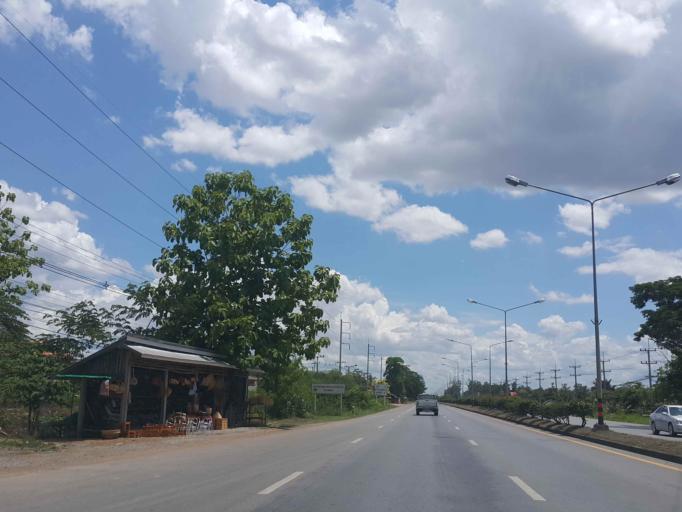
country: TH
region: Phrae
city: Nong Muang Khai
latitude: 18.2488
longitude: 100.2260
